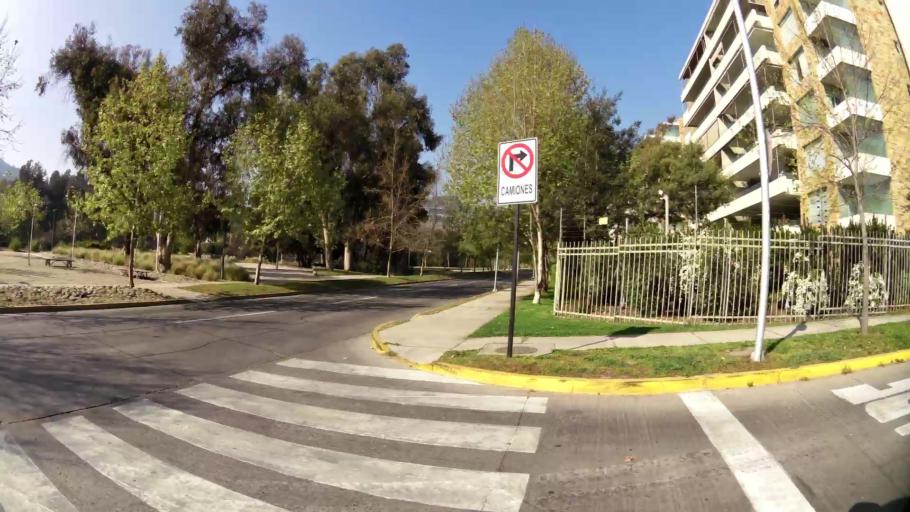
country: CL
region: Santiago Metropolitan
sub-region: Provincia de Santiago
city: Villa Presidente Frei, Nunoa, Santiago, Chile
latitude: -33.3770
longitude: -70.5549
